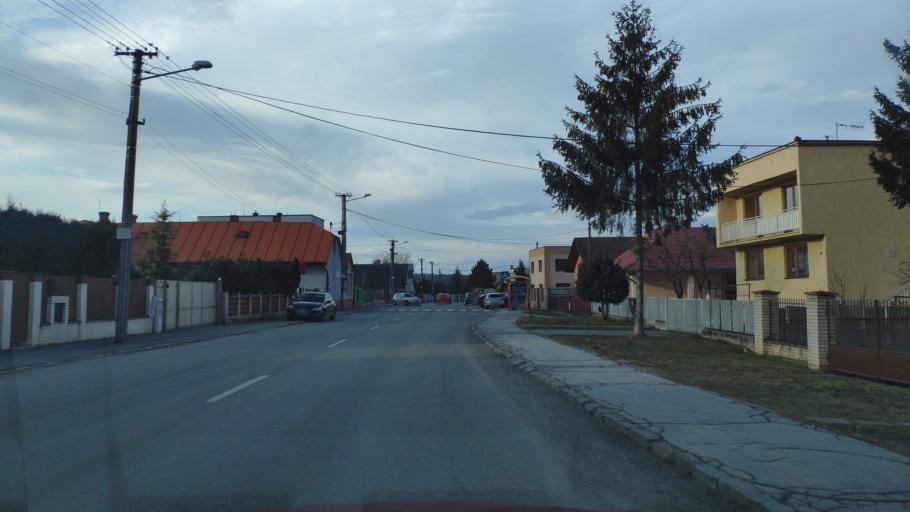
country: SK
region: Kosicky
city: Kosice
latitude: 48.6822
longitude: 21.2616
